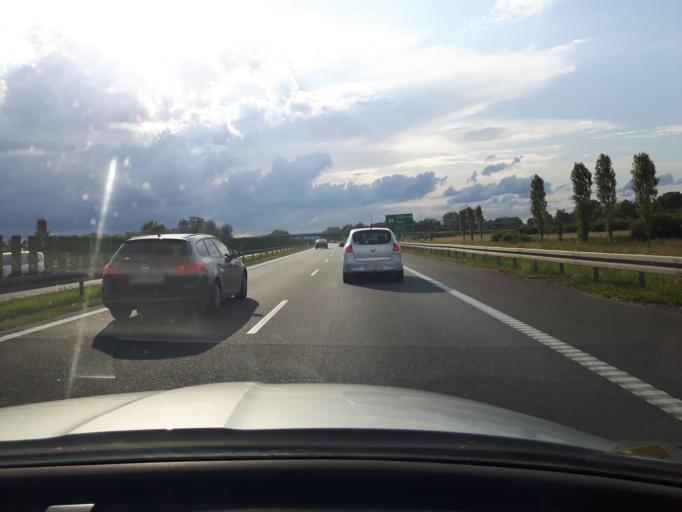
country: PL
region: Pomeranian Voivodeship
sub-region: Gdansk
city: Gdansk
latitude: 54.3196
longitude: 18.7377
